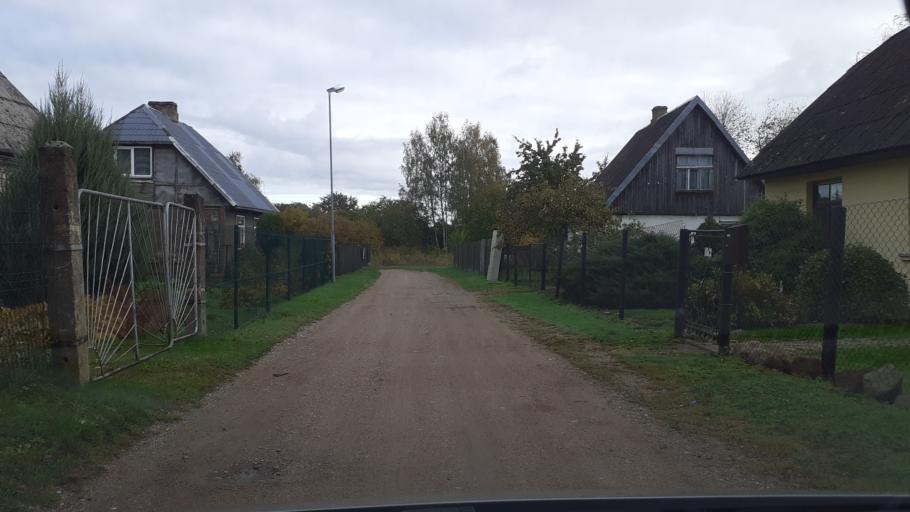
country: LV
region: Kuldigas Rajons
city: Kuldiga
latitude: 56.9640
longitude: 21.9860
